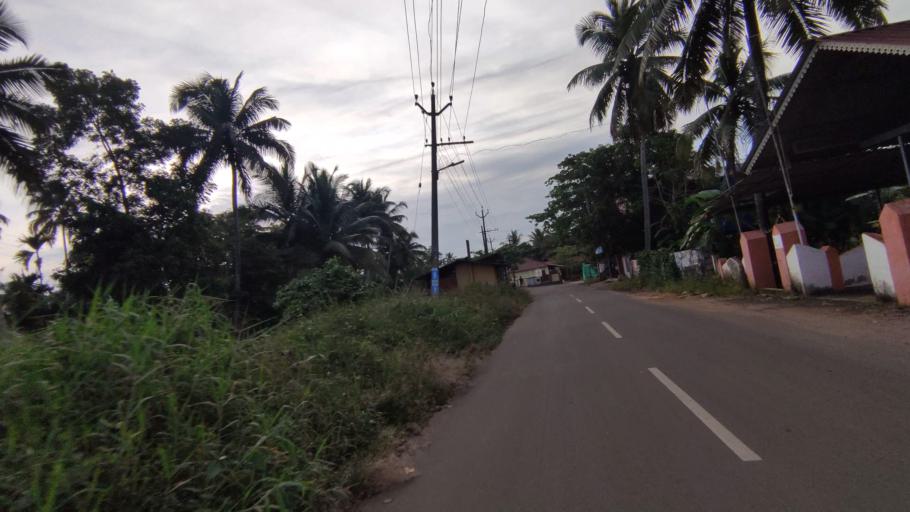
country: IN
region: Kerala
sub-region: Kottayam
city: Kottayam
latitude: 9.6446
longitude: 76.4802
